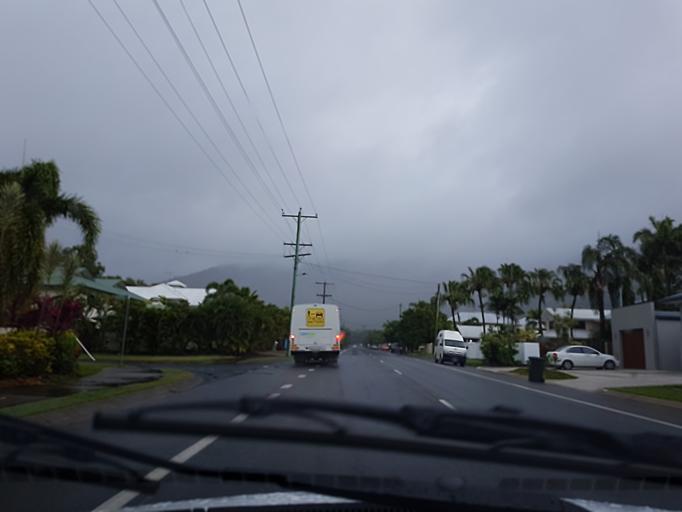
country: AU
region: Queensland
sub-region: Cairns
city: Palm Cove
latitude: -16.7440
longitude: 145.6676
